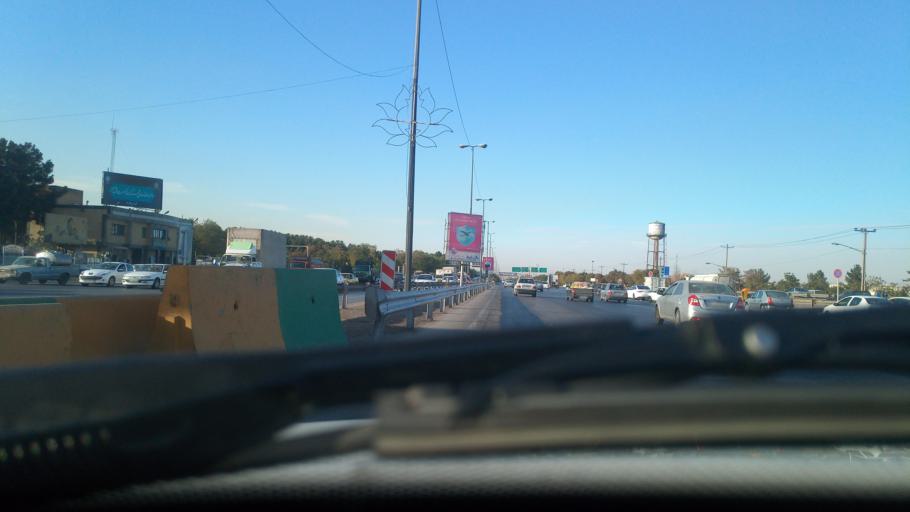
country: IR
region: Razavi Khorasan
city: Mashhad
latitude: 36.2184
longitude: 59.6257
